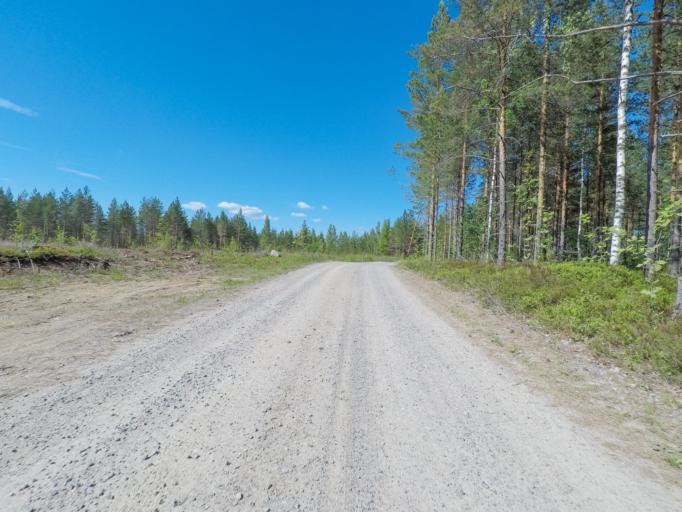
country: FI
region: Northern Savo
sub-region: Varkaus
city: Kangaslampi
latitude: 62.1787
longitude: 28.2221
